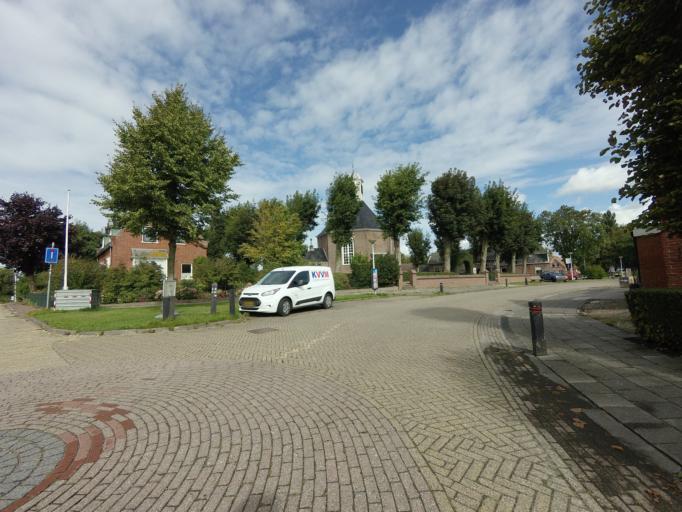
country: NL
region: Friesland
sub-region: Sudwest Fryslan
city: Makkum
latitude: 53.0839
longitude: 5.4237
